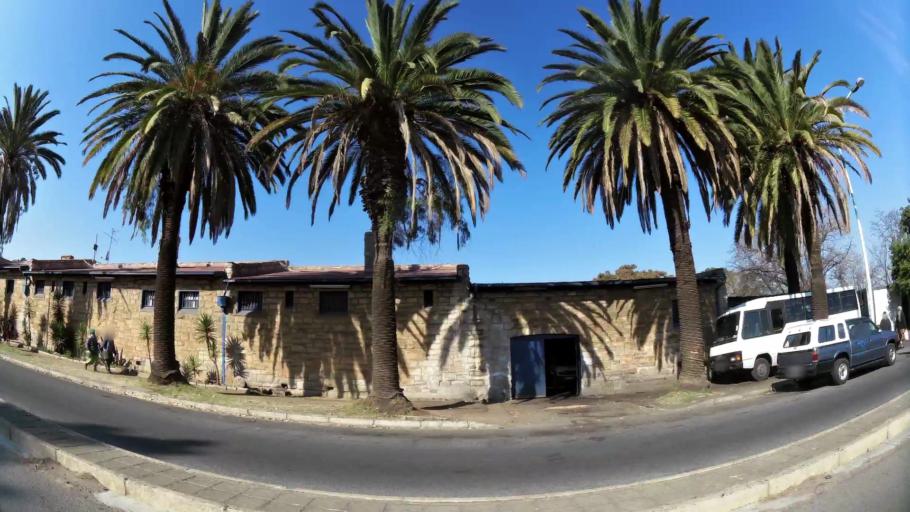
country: ZA
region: Gauteng
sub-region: Ekurhuleni Metropolitan Municipality
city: Boksburg
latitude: -26.2229
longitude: 28.2453
